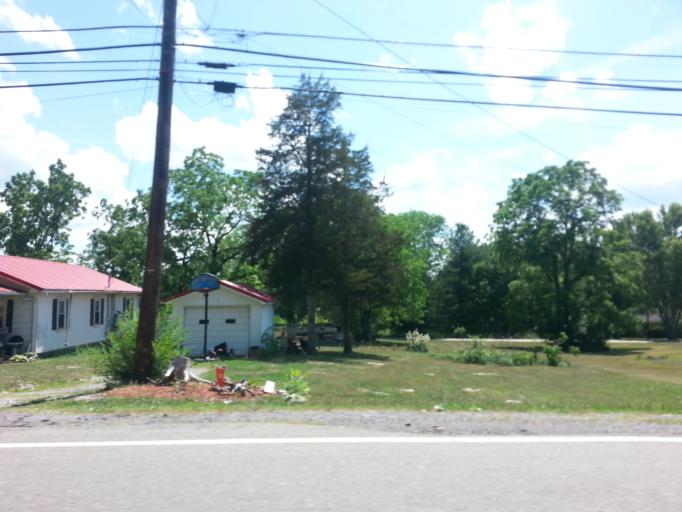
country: US
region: Virginia
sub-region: Lee County
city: Pennington Gap
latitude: 36.7287
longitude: -82.9923
